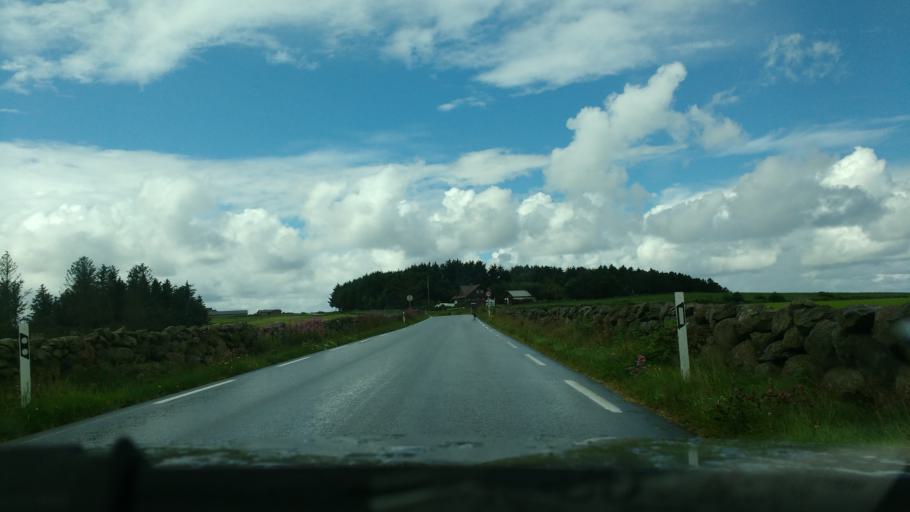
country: NO
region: Rogaland
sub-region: Klepp
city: Kleppe
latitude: 58.7814
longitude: 5.5528
